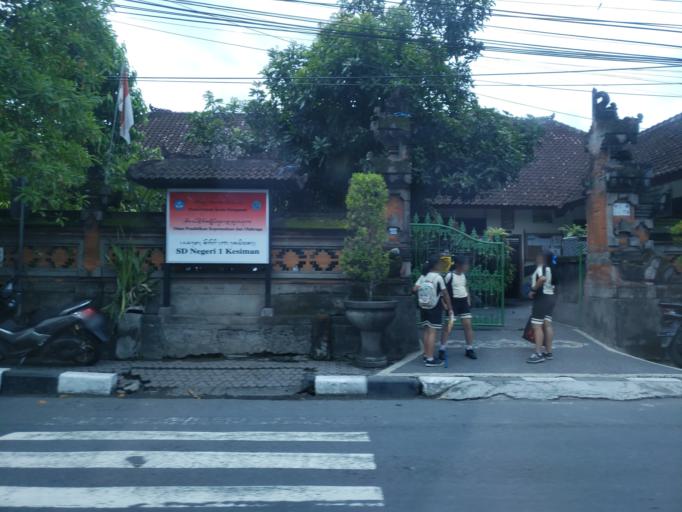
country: ID
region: Bali
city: Dajan Tangluk
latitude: -8.6481
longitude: 115.2405
